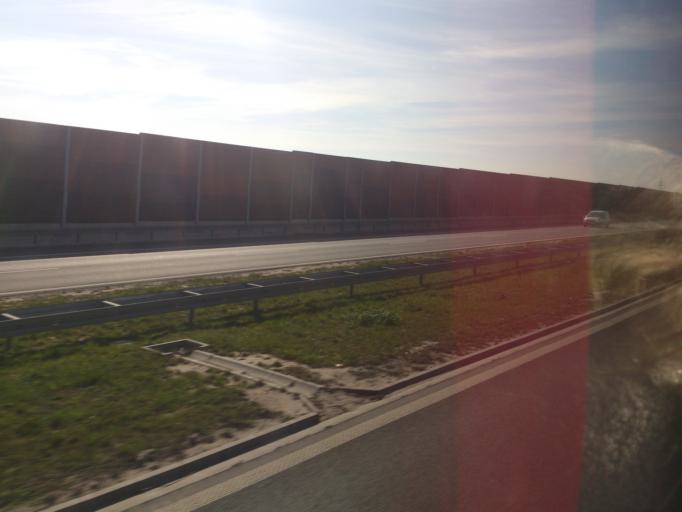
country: PL
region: Kujawsko-Pomorskie
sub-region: Powiat wloclawski
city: Lubanie
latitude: 52.7339
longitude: 18.8594
